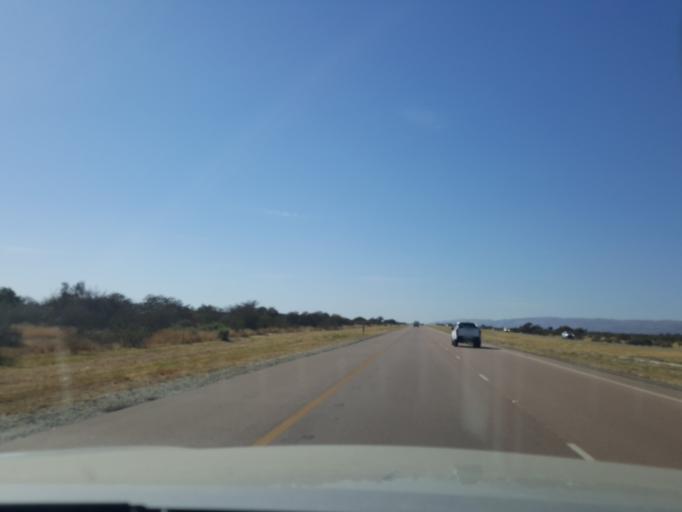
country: ZA
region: North-West
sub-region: Bojanala Platinum District Municipality
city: Brits
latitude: -25.7372
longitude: 27.5715
